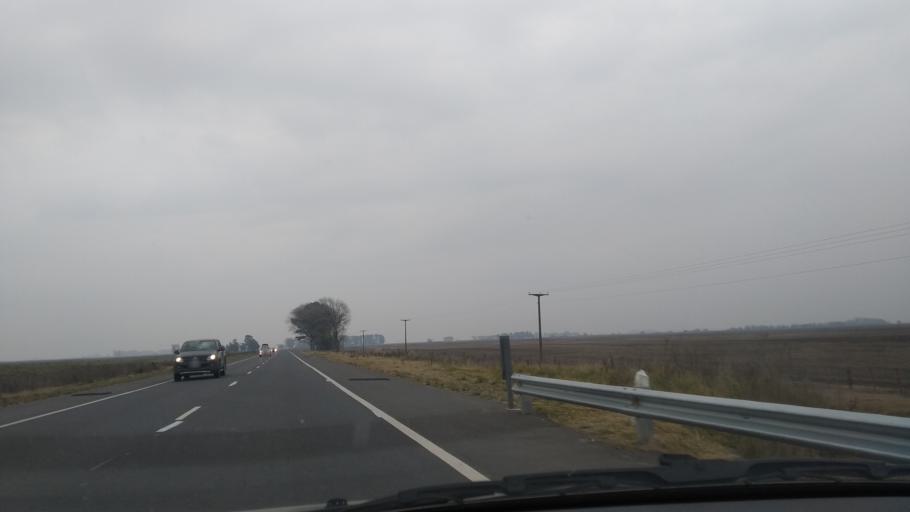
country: AR
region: Buenos Aires
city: Olavarria
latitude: -37.0023
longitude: -60.3600
